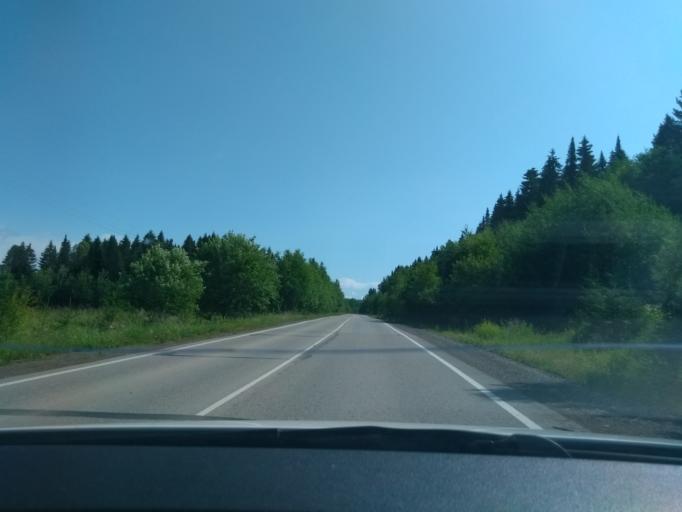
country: RU
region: Perm
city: Bershet'
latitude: 57.8157
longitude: 56.4819
